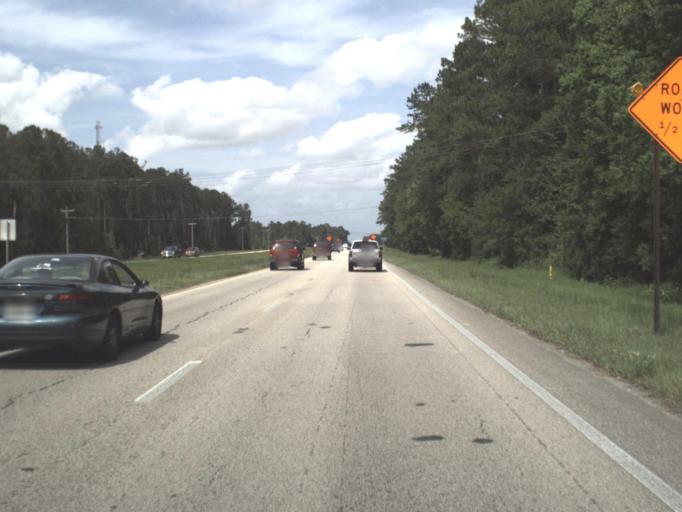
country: US
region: Florida
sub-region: Clay County
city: Middleburg
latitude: 30.0904
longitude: -81.8516
